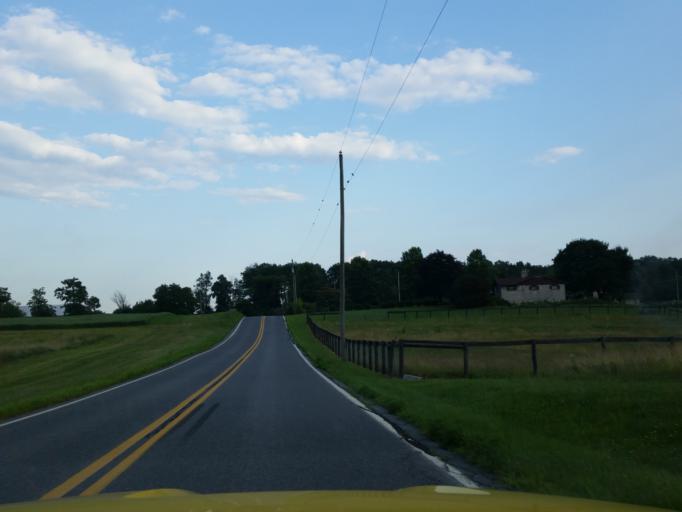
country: US
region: Pennsylvania
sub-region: Lebanon County
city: Palmyra
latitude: 40.4004
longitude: -76.6350
